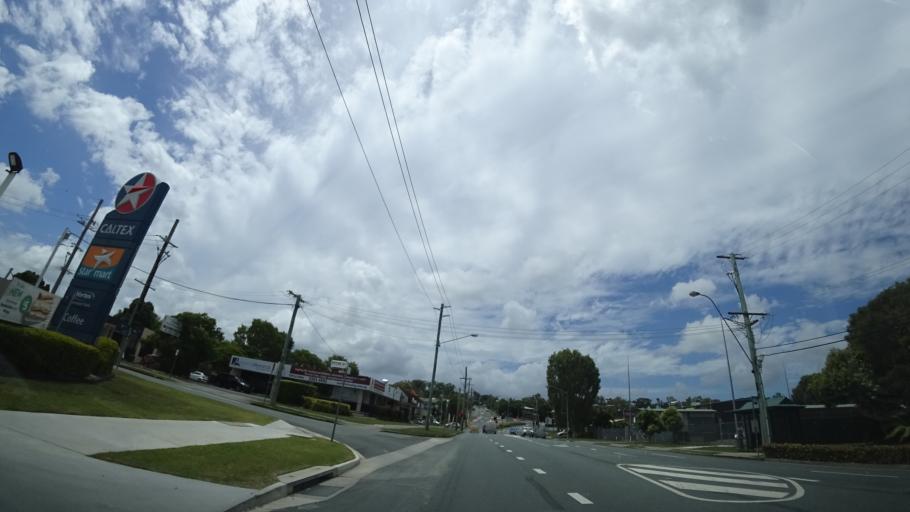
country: AU
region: Queensland
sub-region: Moreton Bay
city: Ferny Hills
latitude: -27.3969
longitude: 152.9611
